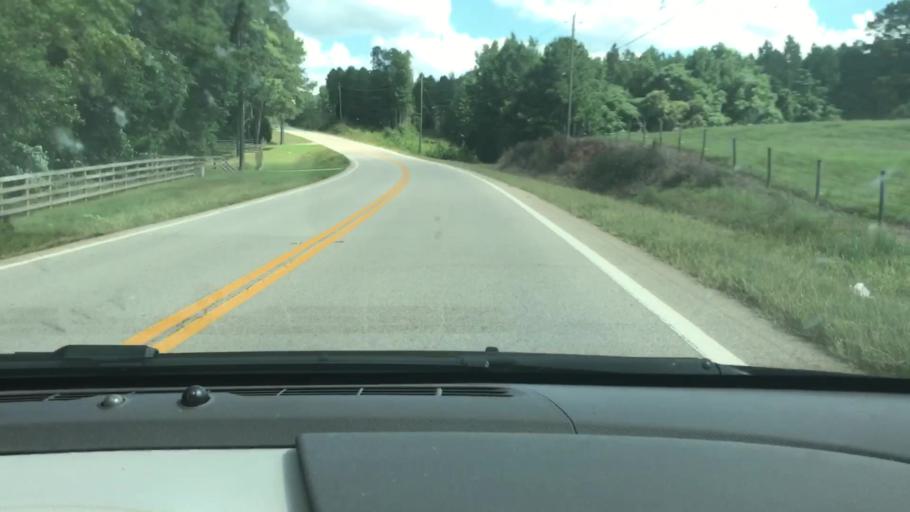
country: US
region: Georgia
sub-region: Troup County
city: La Grange
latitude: 32.9047
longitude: -85.0242
